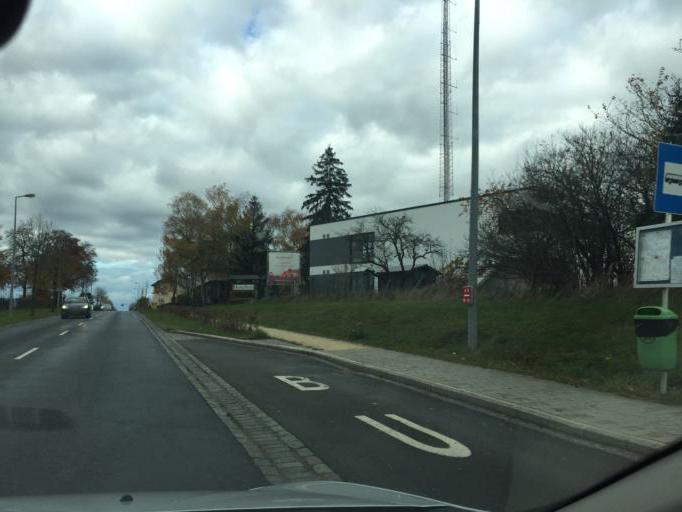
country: LU
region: Diekirch
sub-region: Canton de Wiltz
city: Goesdorf
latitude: 49.8852
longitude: 5.9820
